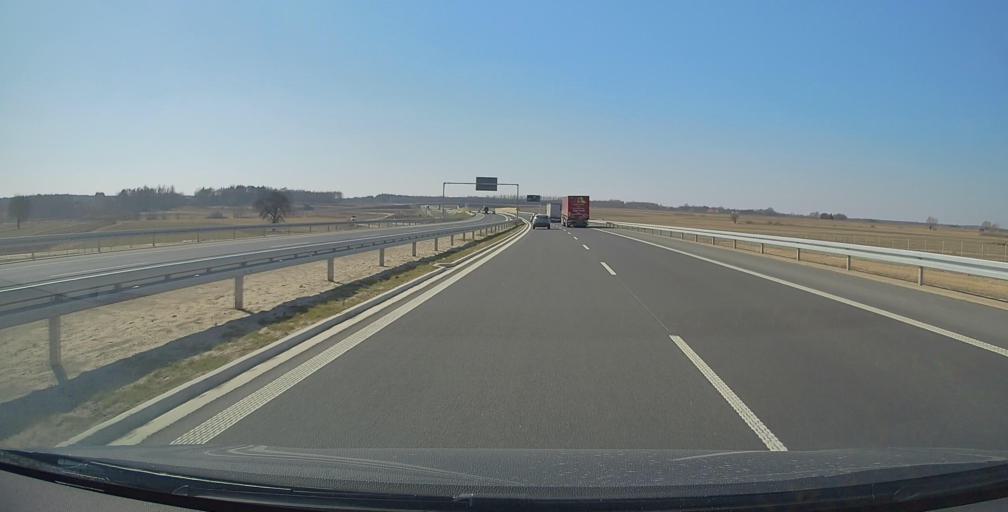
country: PL
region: Subcarpathian Voivodeship
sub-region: Powiat rzeszowski
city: Gorno
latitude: 50.2980
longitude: 22.1211
